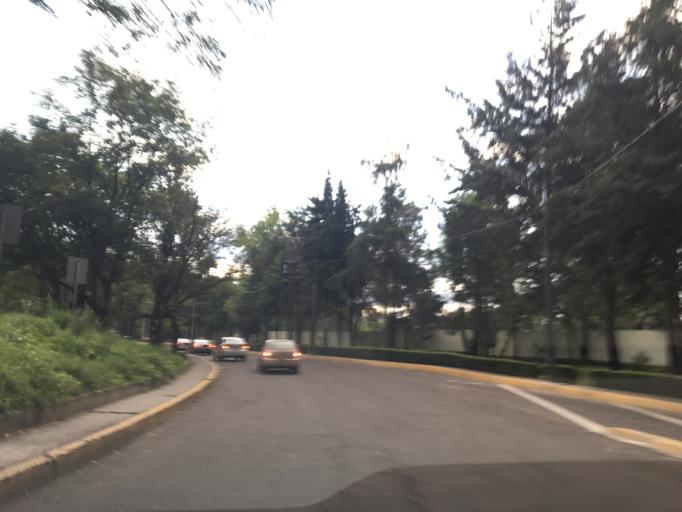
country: MX
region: Mexico City
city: Polanco
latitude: 19.4195
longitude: -99.1944
